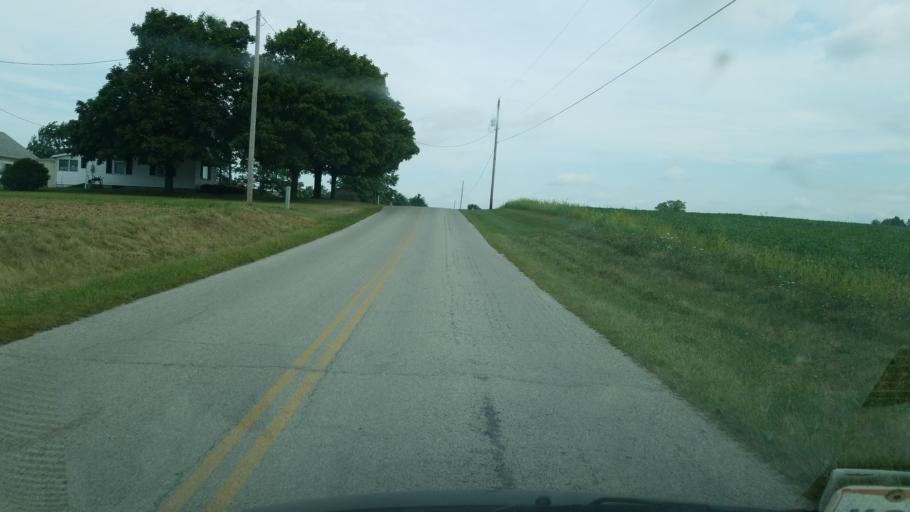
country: US
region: Ohio
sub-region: Seneca County
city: Tiffin
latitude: 41.1057
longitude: -83.0930
